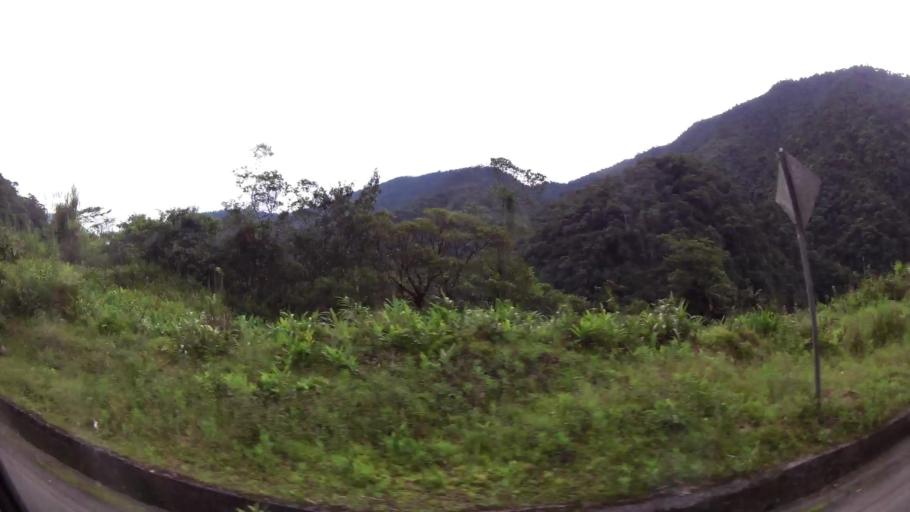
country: EC
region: Pastaza
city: Puyo
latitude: -1.4306
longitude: -78.1767
